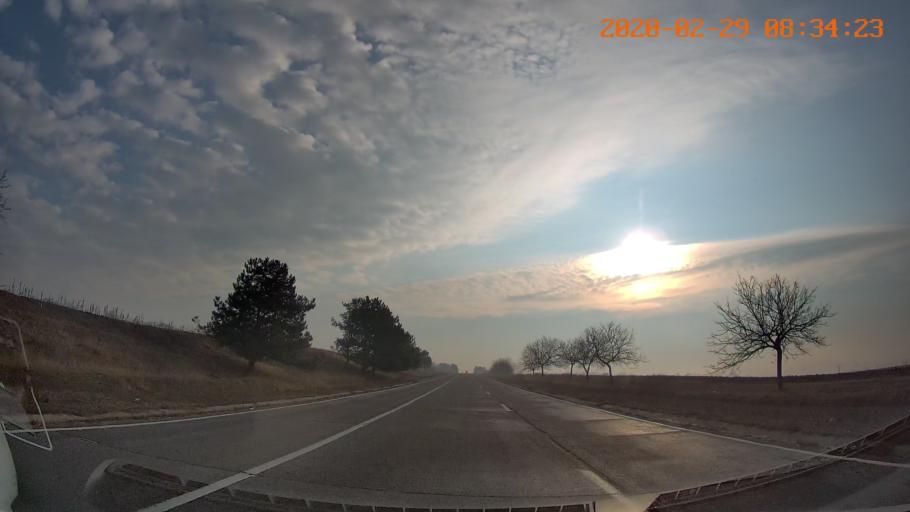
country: MD
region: Anenii Noi
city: Anenii Noi
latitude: 46.9250
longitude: 29.3081
